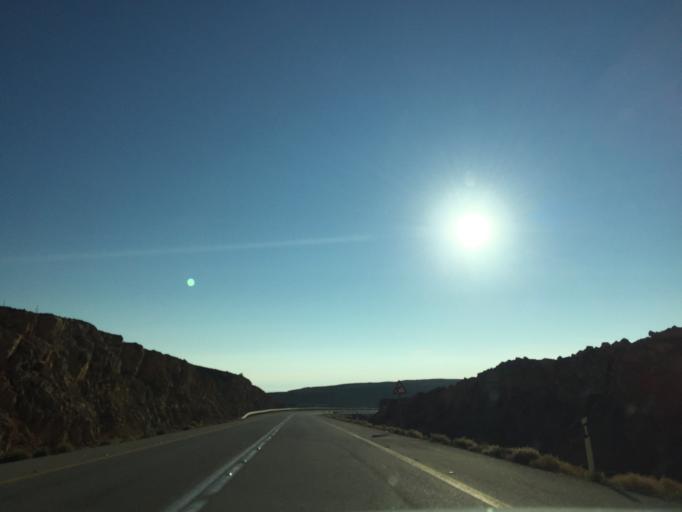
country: IL
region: Southern District
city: Mitzpe Ramon
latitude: 30.5070
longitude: 34.9427
